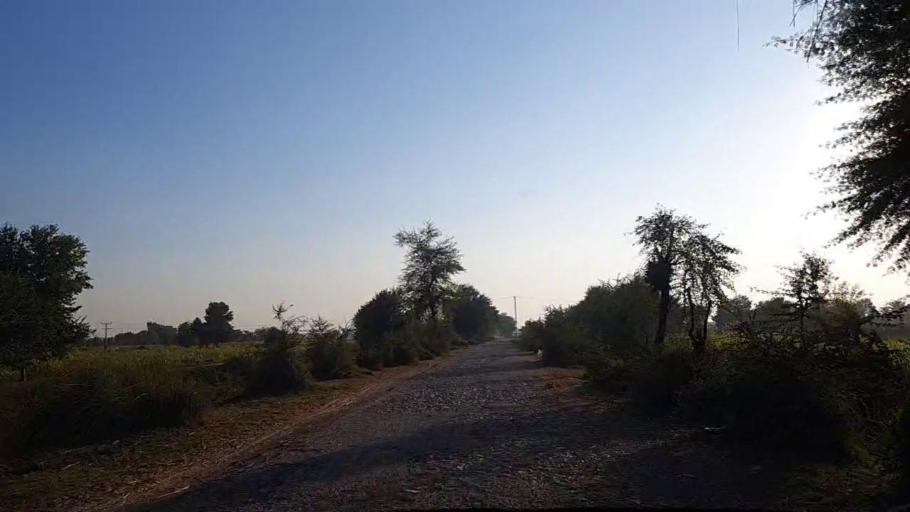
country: PK
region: Sindh
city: Sobhadero
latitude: 27.4014
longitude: 68.3897
